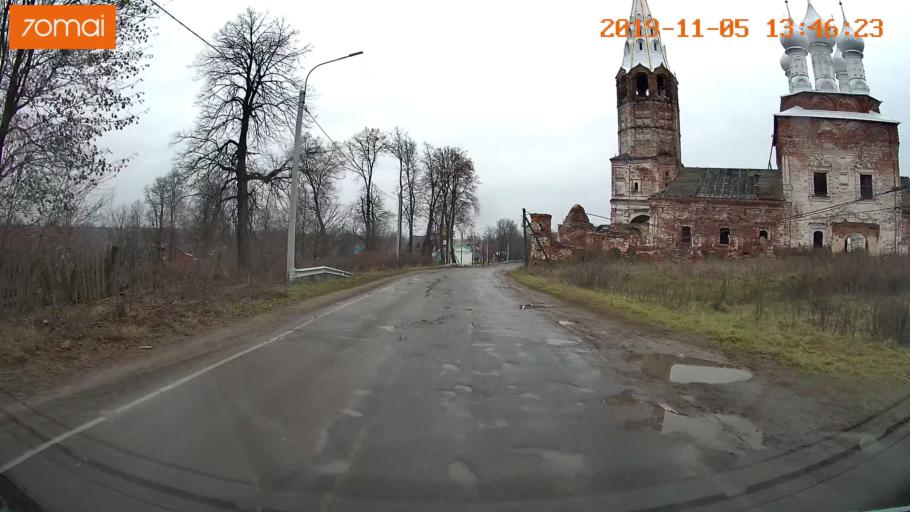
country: RU
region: Ivanovo
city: Shuya
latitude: 56.9951
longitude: 41.4100
